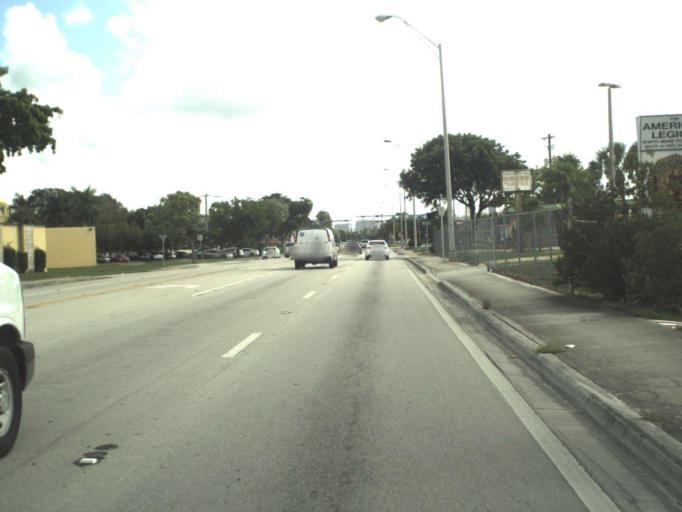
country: US
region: Florida
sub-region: Miami-Dade County
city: North Miami Beach
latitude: 25.9133
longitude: -80.1649
